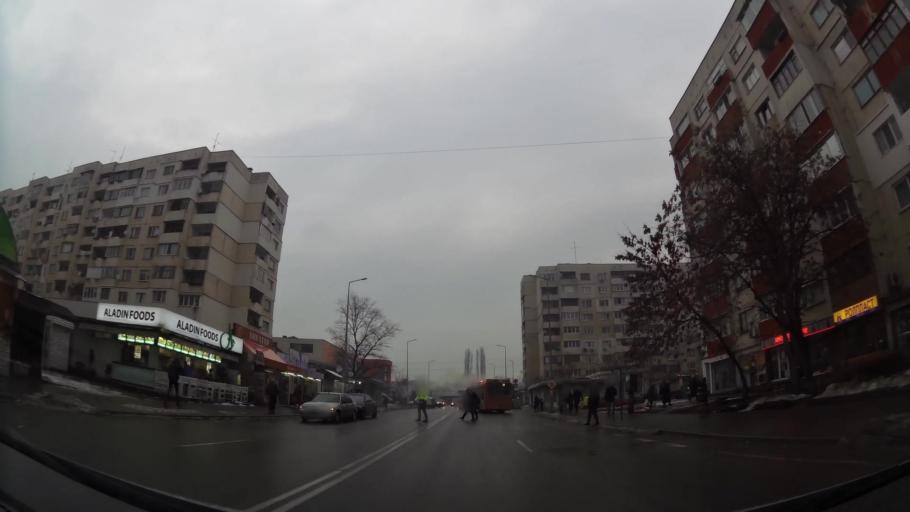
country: BG
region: Sofia-Capital
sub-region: Stolichna Obshtina
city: Sofia
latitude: 42.6893
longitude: 23.2548
